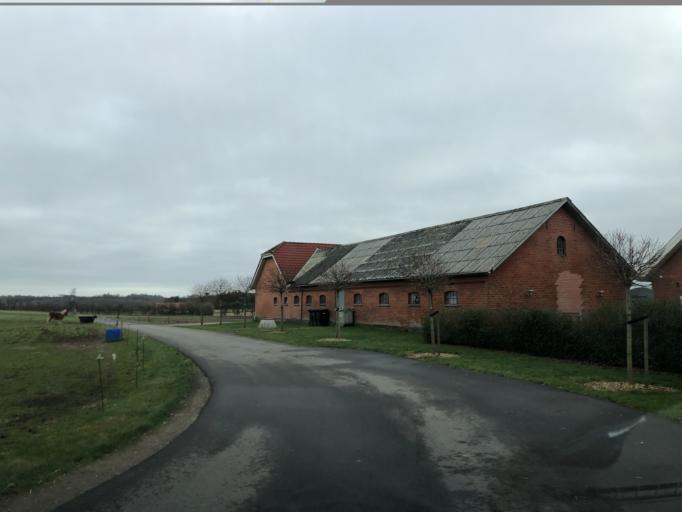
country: DK
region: Central Jutland
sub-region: Viborg Kommune
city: Stoholm
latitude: 56.4508
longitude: 9.1188
